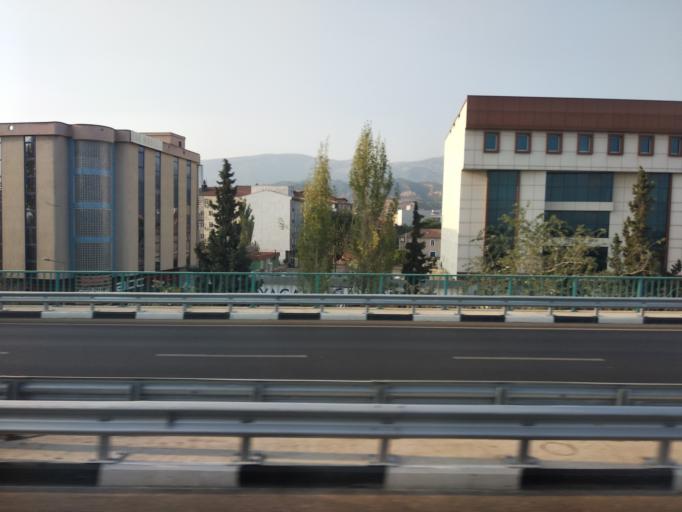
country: TR
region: Manisa
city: Salihli
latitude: 38.4903
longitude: 28.1402
